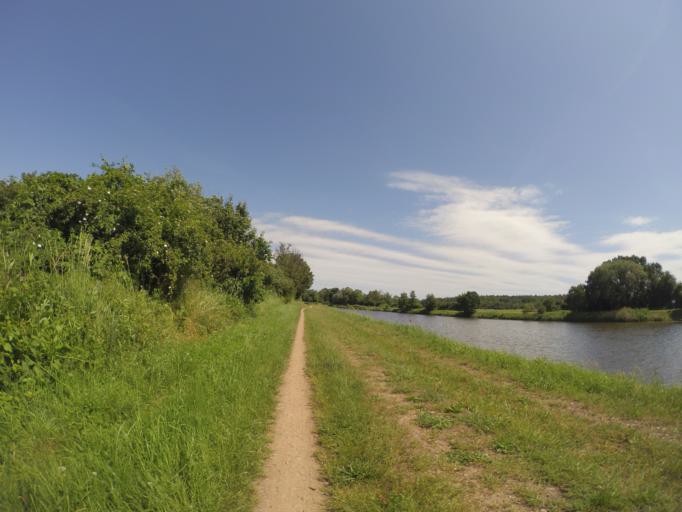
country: CZ
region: Central Bohemia
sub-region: Okres Nymburk
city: Sadska
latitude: 50.1626
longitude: 14.9627
